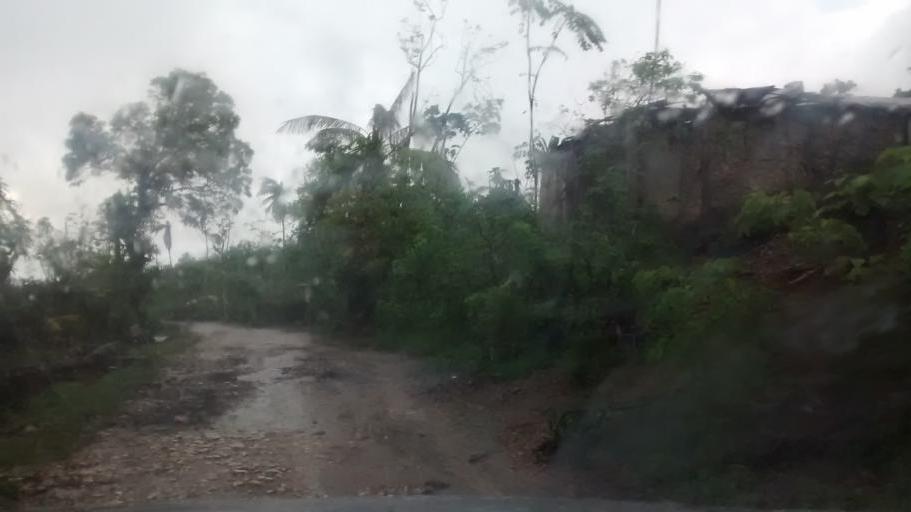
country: HT
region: Grandans
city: Corail
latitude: 18.5319
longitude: -73.9506
